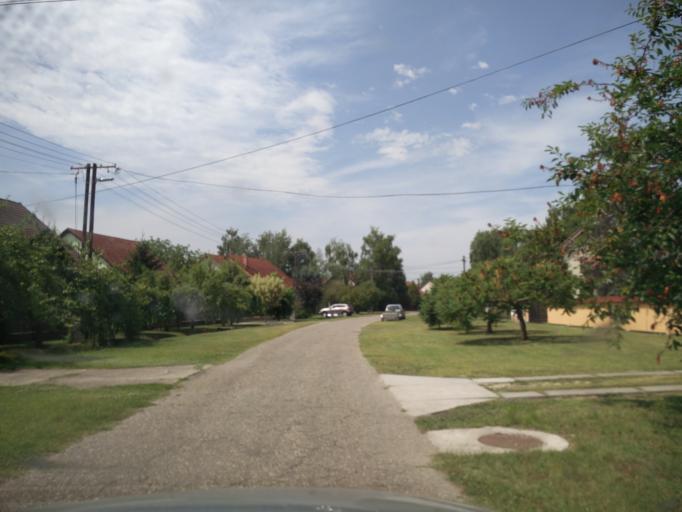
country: HU
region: Csongrad
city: Sandorfalva
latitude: 46.3644
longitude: 20.1073
